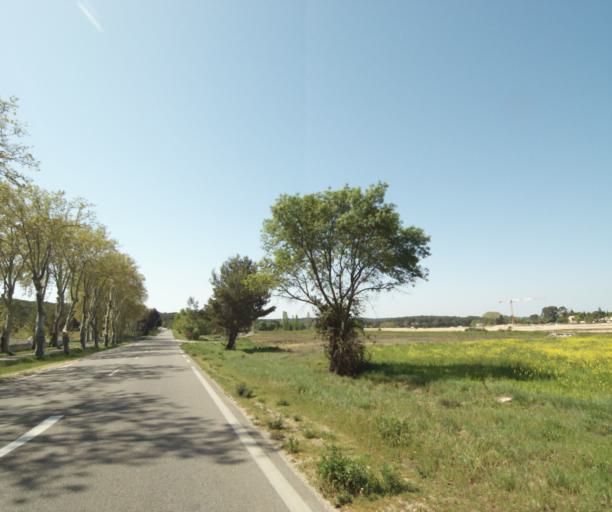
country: FR
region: Languedoc-Roussillon
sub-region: Departement de l'Herault
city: Clapiers
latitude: 43.6573
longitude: 3.8994
